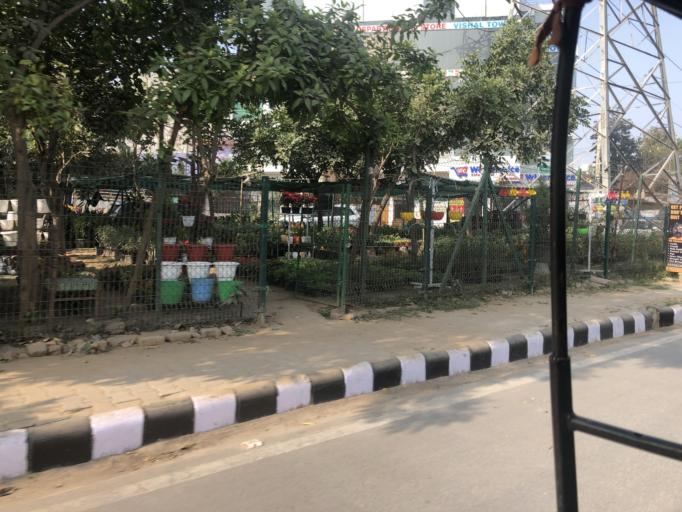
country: IN
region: Haryana
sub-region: Gurgaon
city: Gurgaon
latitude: 28.4363
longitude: 77.0902
